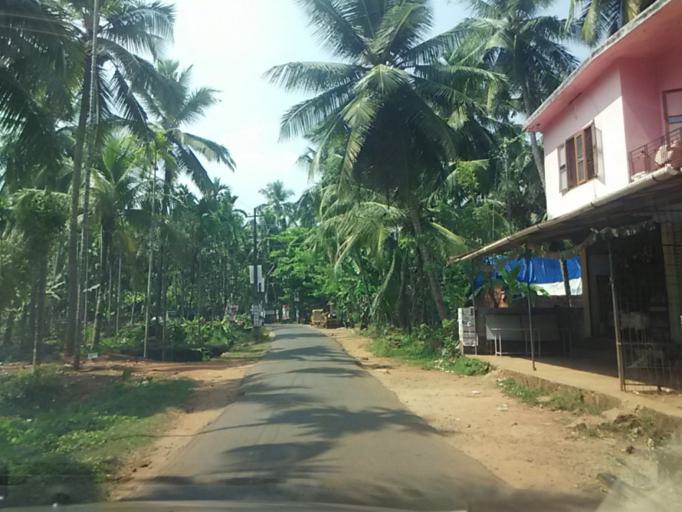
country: IN
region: Kerala
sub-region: Kozhikode
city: Naduvannur
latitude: 11.5402
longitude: 75.7560
